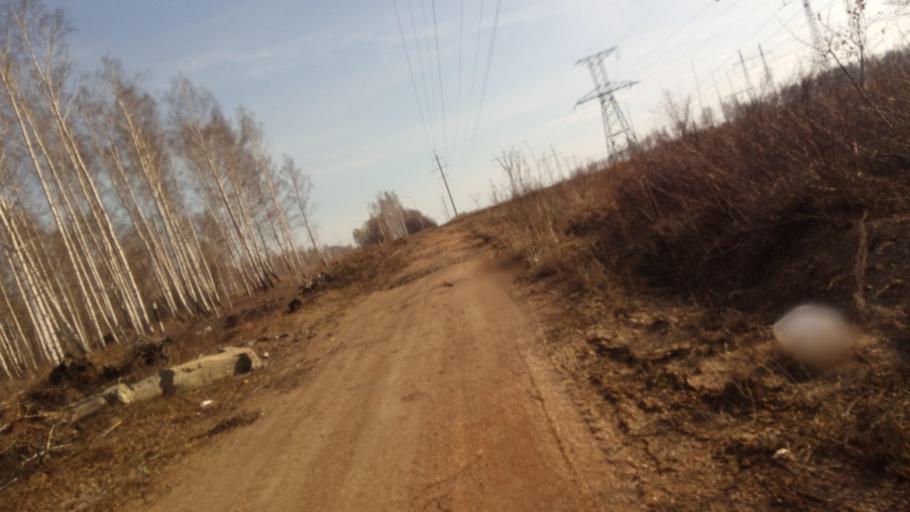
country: RU
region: Chelyabinsk
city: Sargazy
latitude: 55.1163
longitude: 61.2360
